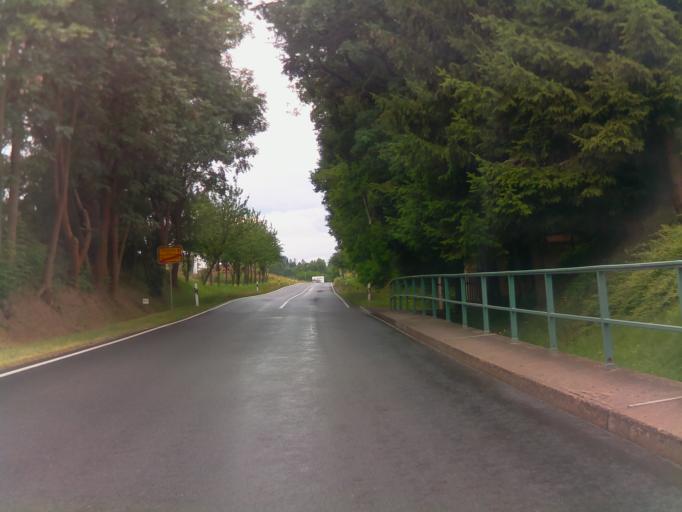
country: DE
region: Thuringia
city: Langewiesen
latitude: 50.7080
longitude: 10.9737
